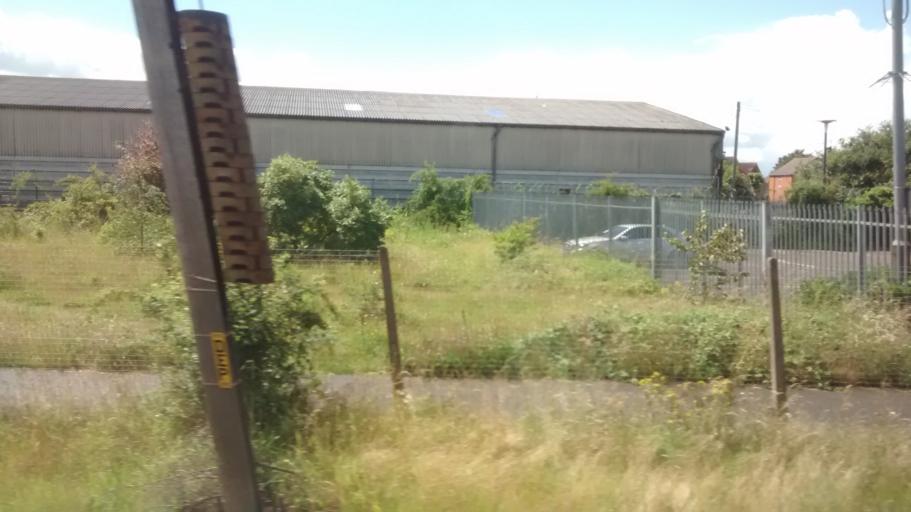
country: GB
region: England
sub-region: Nottinghamshire
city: Newark on Trent
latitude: 53.0791
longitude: -0.7982
